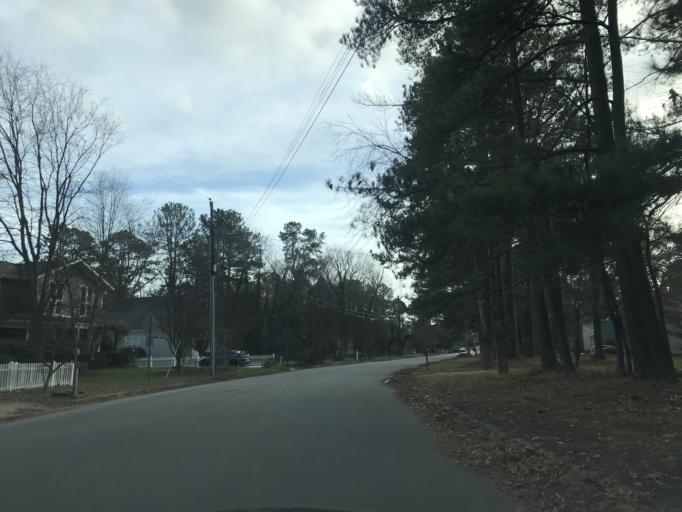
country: US
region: North Carolina
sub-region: Wake County
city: Raleigh
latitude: 35.7957
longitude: -78.6176
